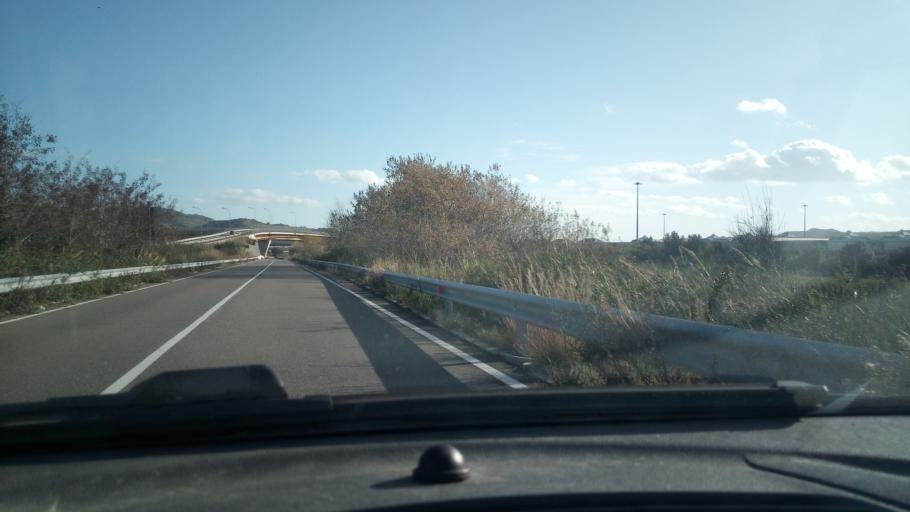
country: IT
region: Calabria
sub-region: Provincia di Catanzaro
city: Catanzaro
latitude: 38.8573
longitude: 16.5718
